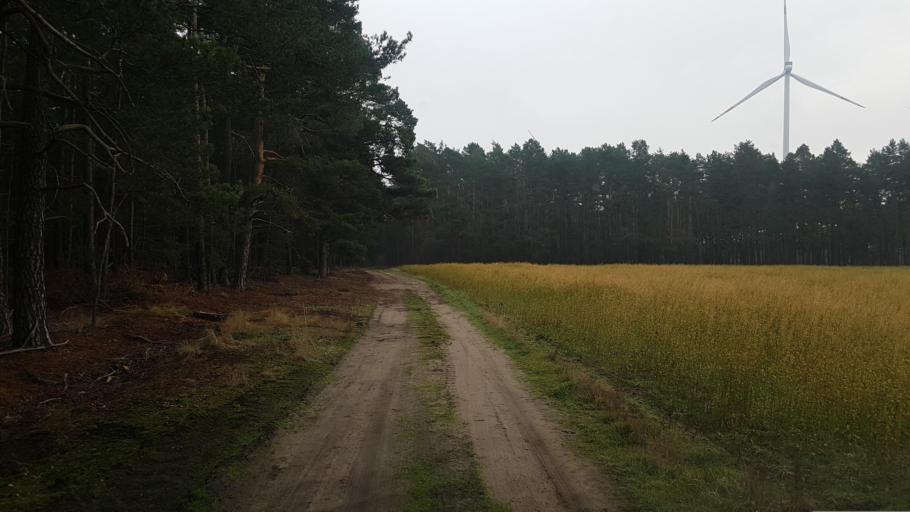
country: DE
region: Brandenburg
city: Sallgast
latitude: 51.6520
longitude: 13.8194
